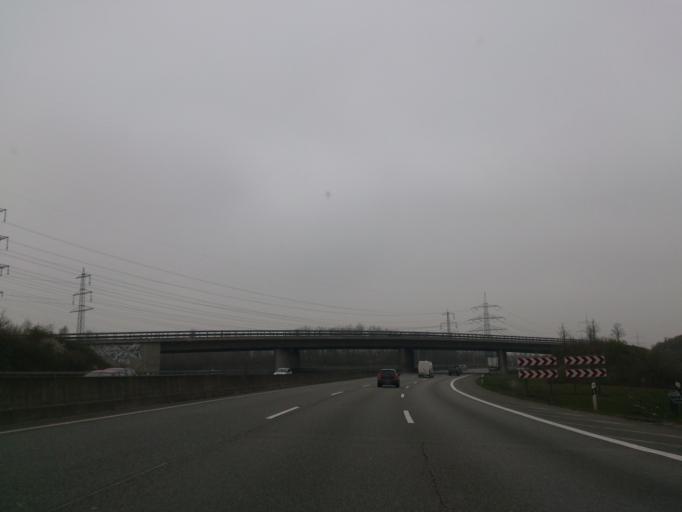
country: DE
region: North Rhine-Westphalia
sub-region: Regierungsbezirk Dusseldorf
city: Neuss
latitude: 51.1799
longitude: 6.6710
